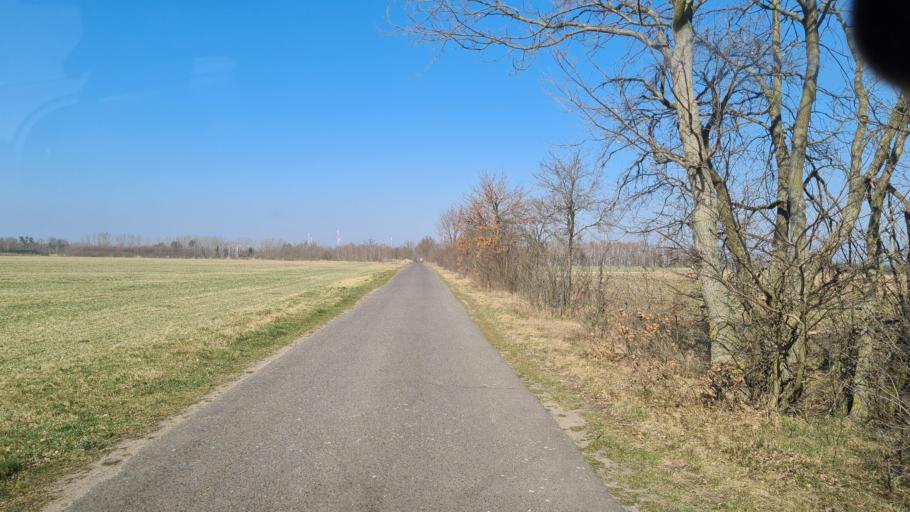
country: DE
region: Brandenburg
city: Calau
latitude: 51.7949
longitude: 13.9860
